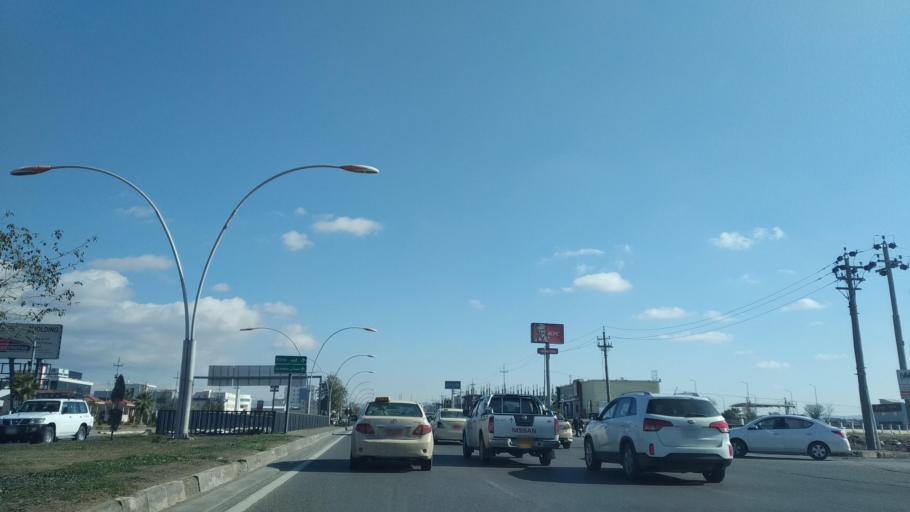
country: IQ
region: Arbil
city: Erbil
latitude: 36.1980
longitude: 44.0732
